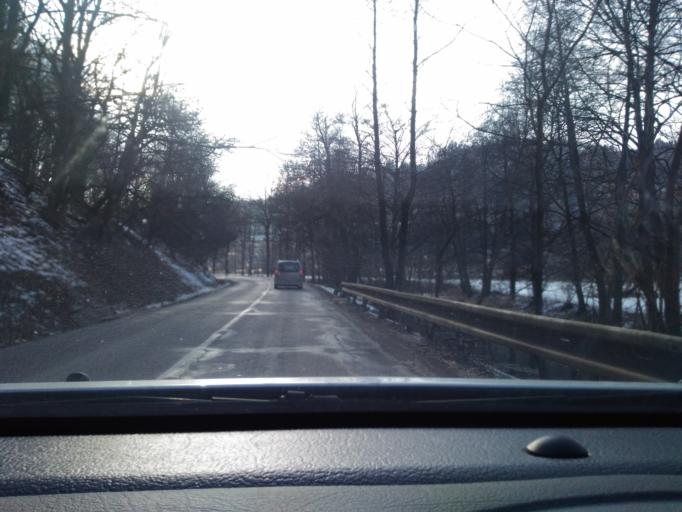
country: CZ
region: South Moravian
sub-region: Okres Brno-Venkov
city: Nedvedice
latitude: 49.4627
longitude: 16.3362
